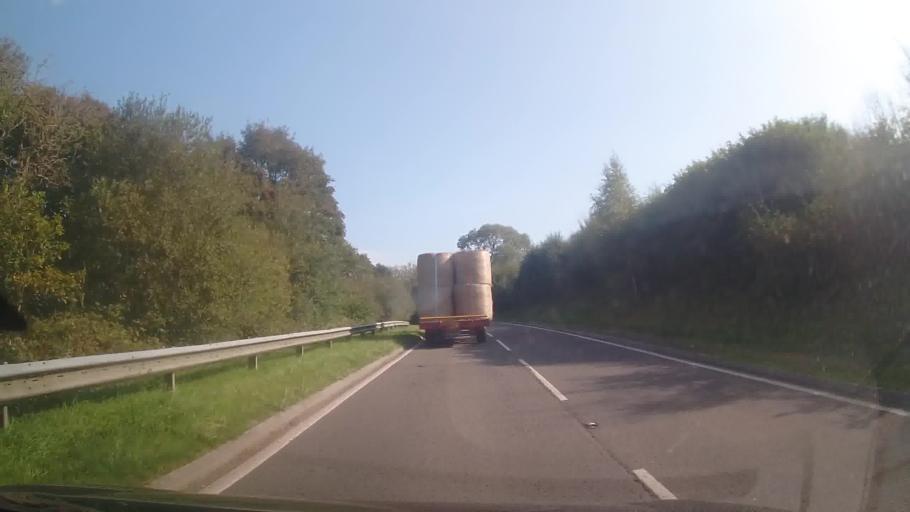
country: GB
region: Wales
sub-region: Pembrokeshire
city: Nevern
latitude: 52.0150
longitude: -4.7795
